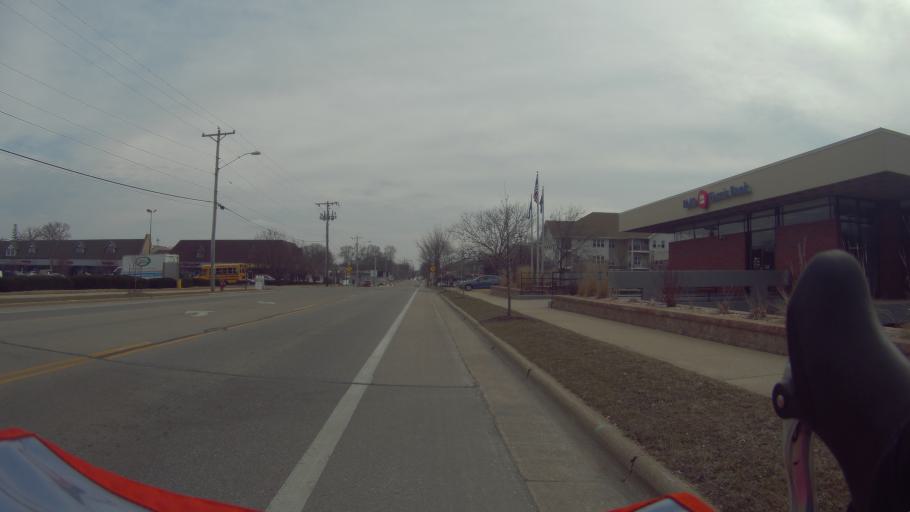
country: US
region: Wisconsin
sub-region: Dane County
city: Maple Bluff
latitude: 43.1132
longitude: -89.3639
